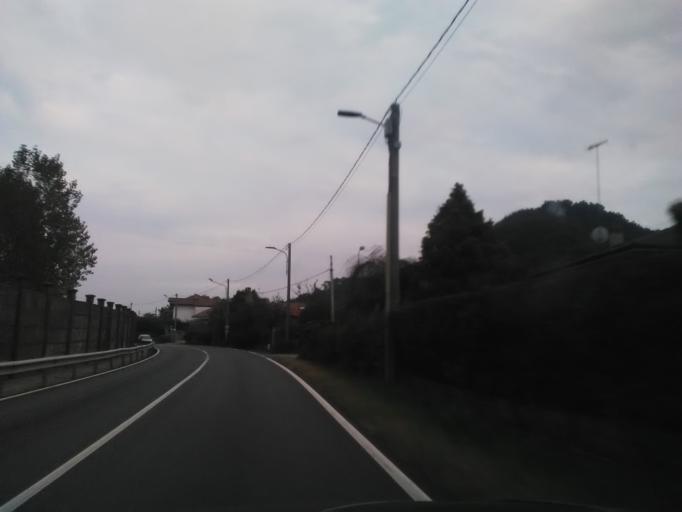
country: IT
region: Piedmont
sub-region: Provincia di Vercelli
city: Serravalle Sesia
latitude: 45.6858
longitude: 8.3060
